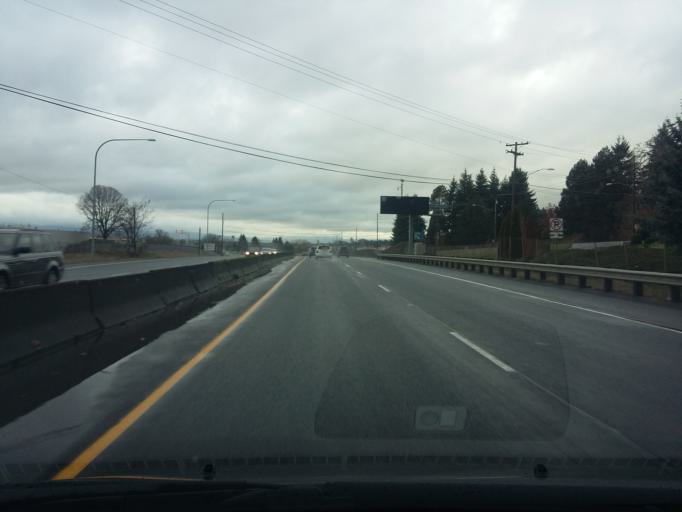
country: US
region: Washington
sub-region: Clark County
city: Vancouver
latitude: 45.6182
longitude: -122.6232
